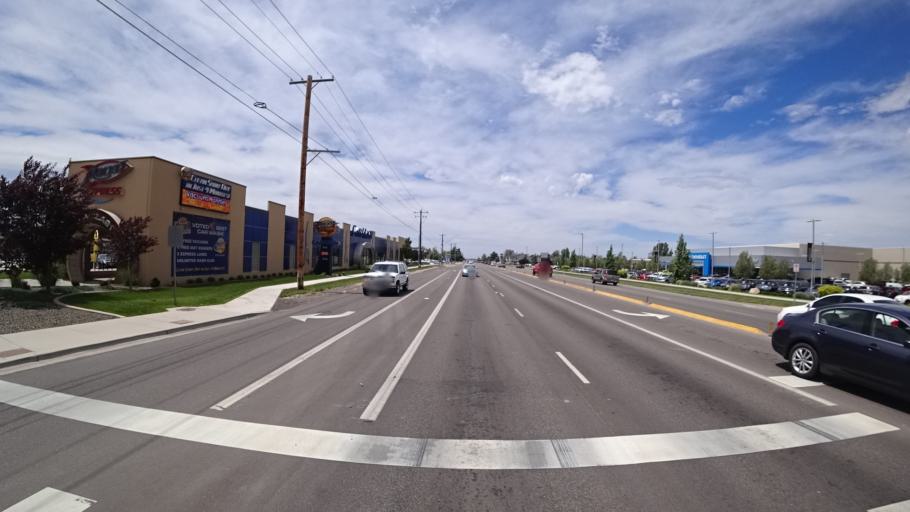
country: US
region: Idaho
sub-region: Ada County
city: Meridian
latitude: 43.6194
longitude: -116.3349
